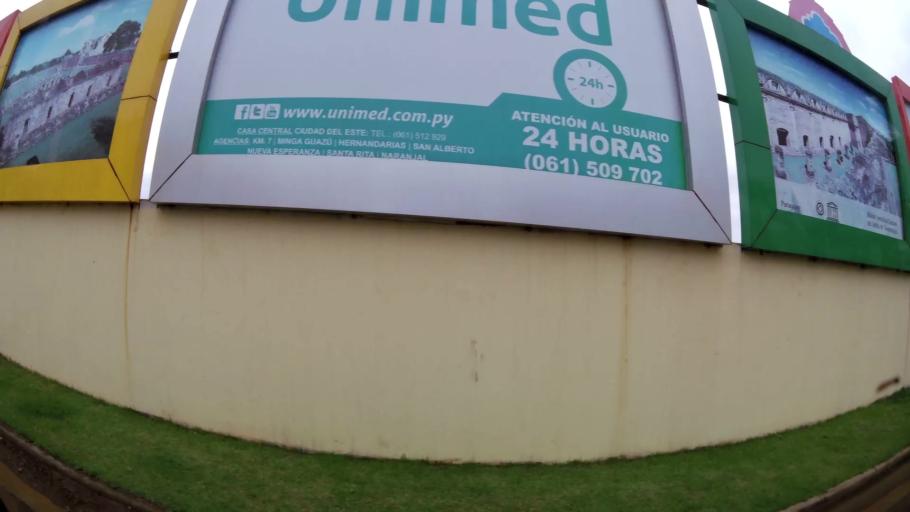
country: PY
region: Alto Parana
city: Ciudad del Este
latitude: -25.4979
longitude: -54.6795
